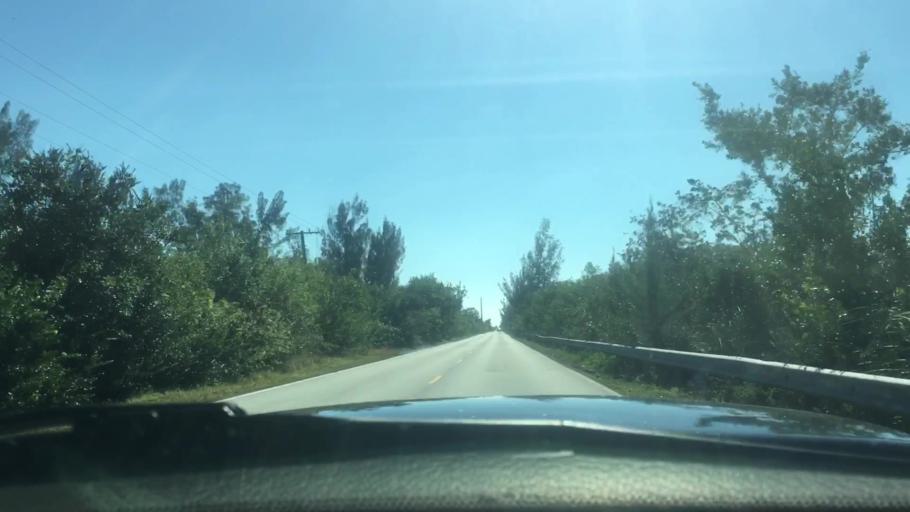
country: US
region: Florida
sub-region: Miami-Dade County
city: Florida City
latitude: 25.3673
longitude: -80.4301
